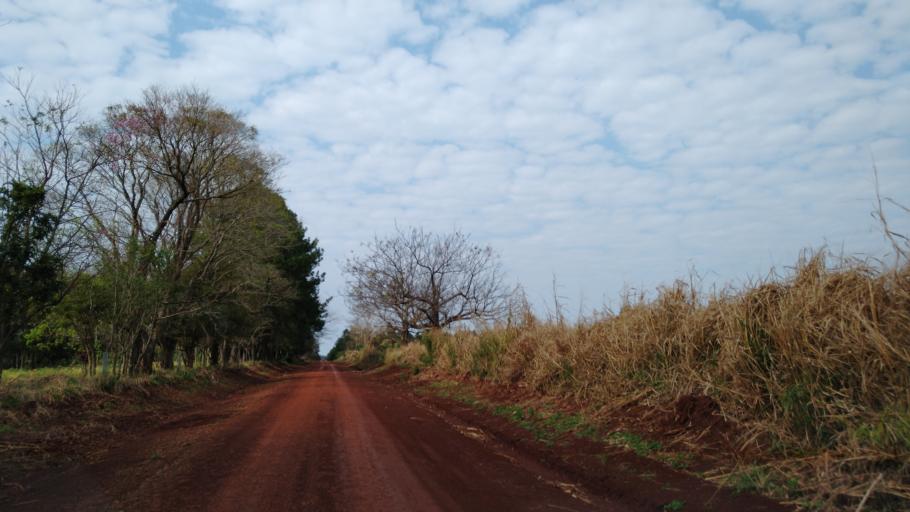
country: AR
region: Misiones
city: Capiovi
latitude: -26.9564
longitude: -55.0618
